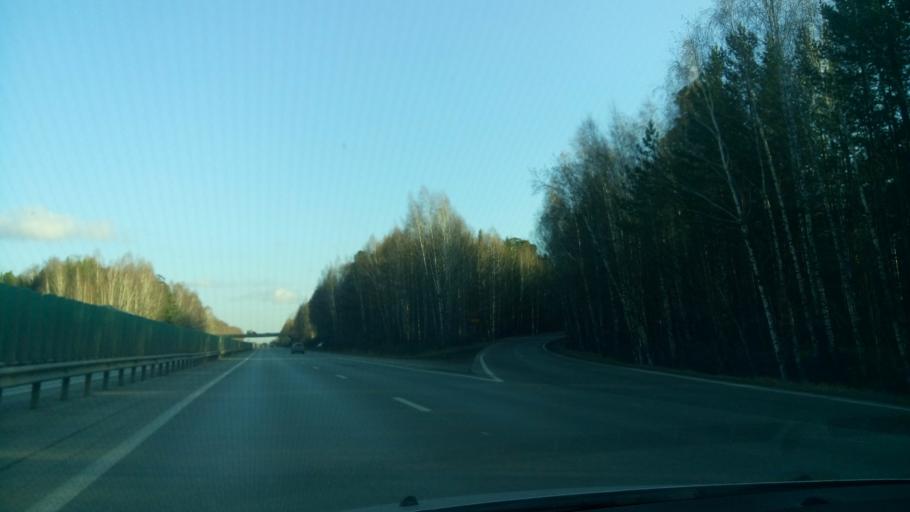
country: RU
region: Sverdlovsk
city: Aramil
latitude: 56.7747
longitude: 60.8669
